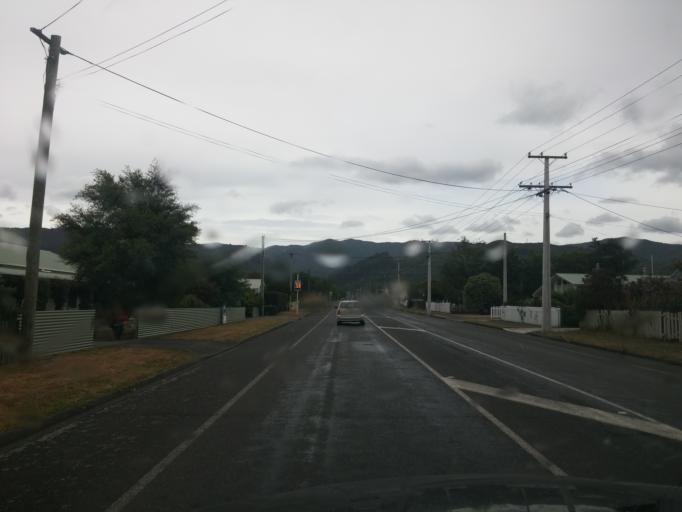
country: NZ
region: Wellington
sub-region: Upper Hutt City
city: Upper Hutt
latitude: -41.1210
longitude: 175.3296
